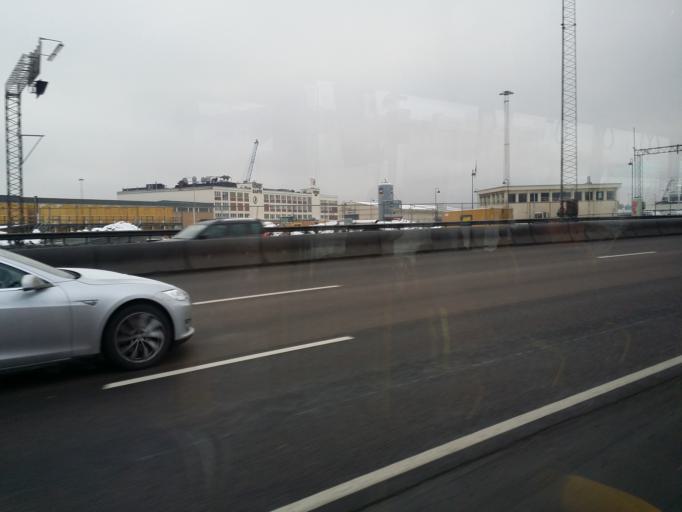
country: NO
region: Oslo
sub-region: Oslo
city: Oslo
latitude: 59.9099
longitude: 10.7156
